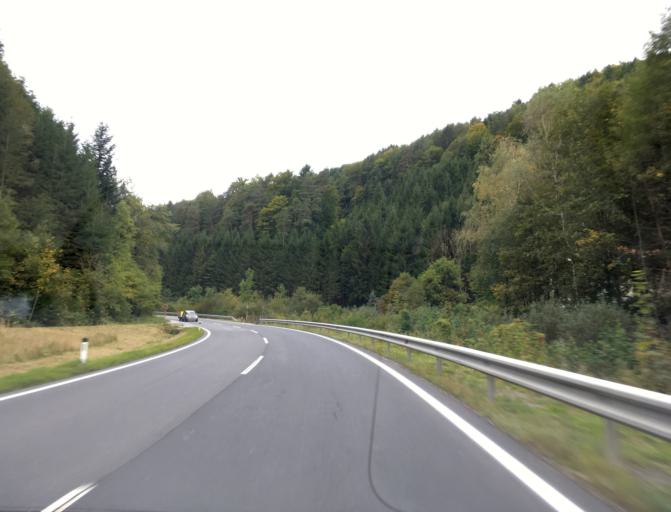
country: AT
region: Lower Austria
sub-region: Politischer Bezirk Neunkirchen
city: Edlitz
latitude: 47.5805
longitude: 16.1429
